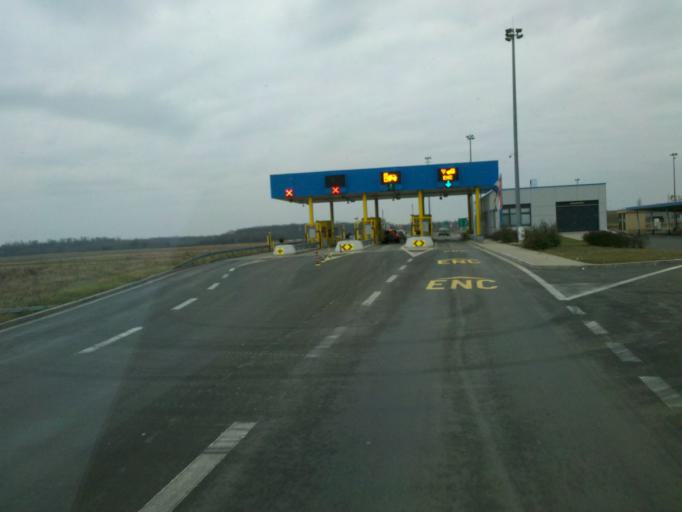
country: HR
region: Grad Zagreb
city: Horvati
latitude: 45.6754
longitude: 15.7576
